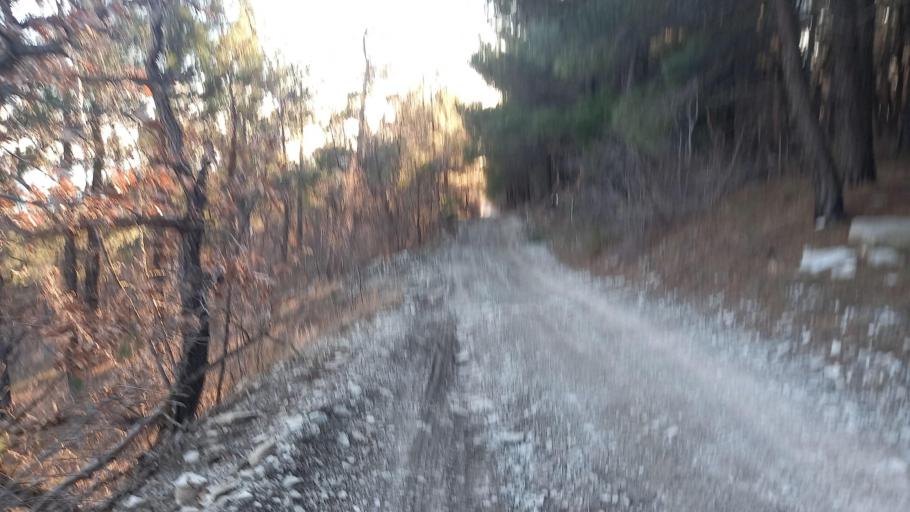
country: RU
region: Krasnodarskiy
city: Kabardinka
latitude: 44.6180
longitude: 37.9311
